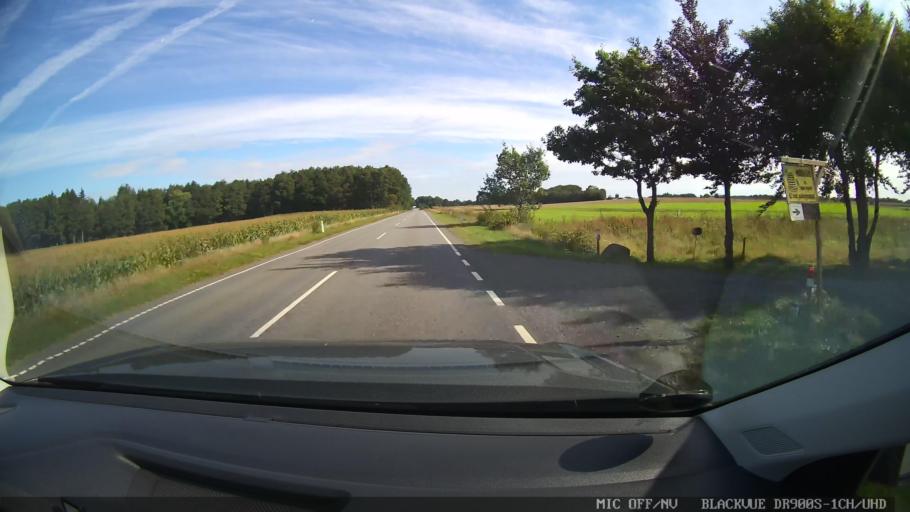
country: DK
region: North Denmark
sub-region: Mariagerfjord Kommune
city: Hadsund
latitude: 56.7858
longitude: 10.0193
